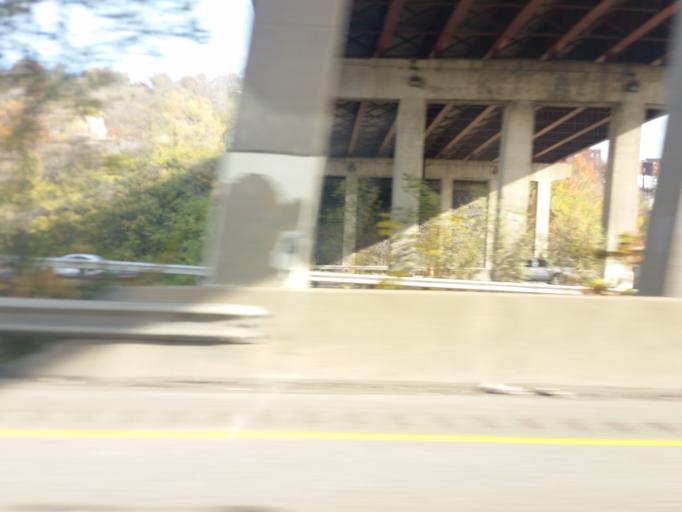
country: US
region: Kentucky
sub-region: Kenton County
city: Ludlow
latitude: 39.1246
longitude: -84.5354
